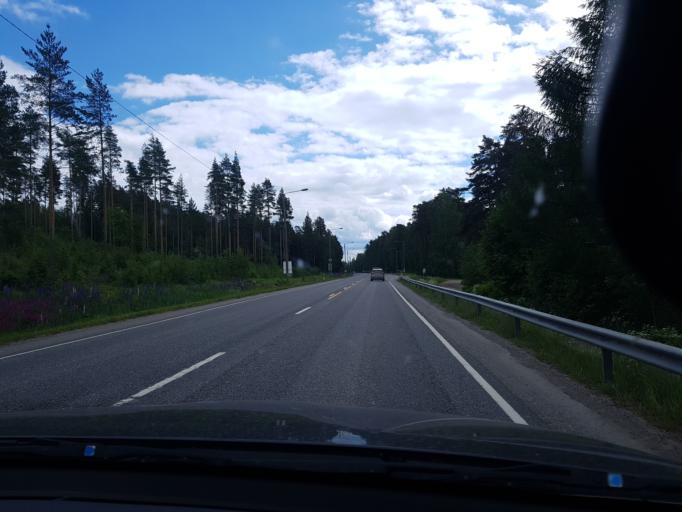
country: FI
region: Pirkanmaa
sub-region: Tampere
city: Paelkaene
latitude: 61.3008
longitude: 24.3033
